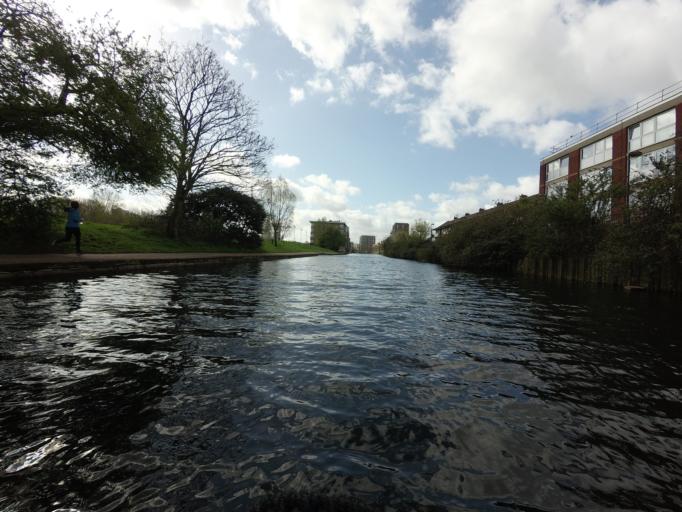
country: GB
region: England
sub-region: Greater London
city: Poplar
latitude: 51.5224
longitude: -0.0365
